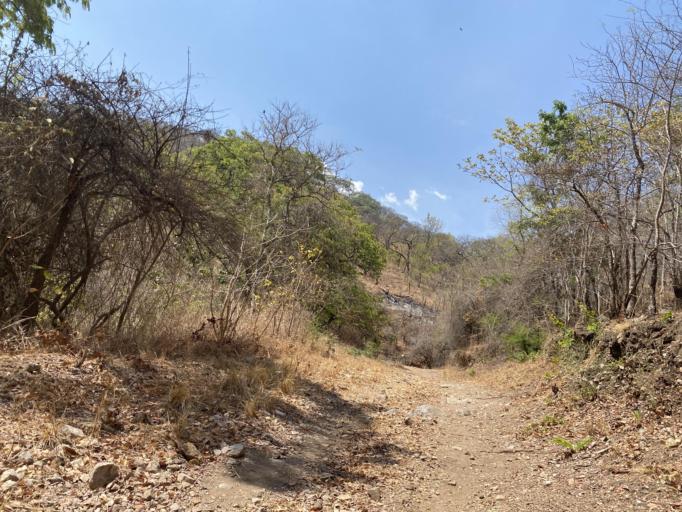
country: ZM
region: Lusaka
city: Kafue
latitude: -15.7418
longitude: 28.4742
